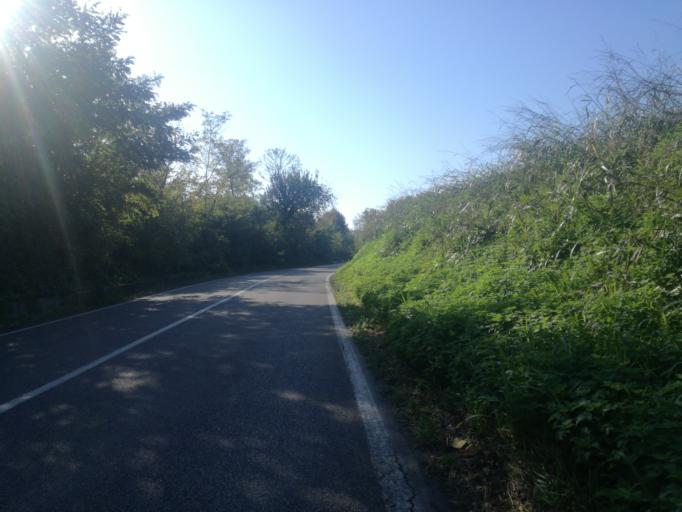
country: IT
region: Lombardy
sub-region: Provincia di Monza e Brianza
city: Cornate d'Adda
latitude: 45.6400
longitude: 9.4872
